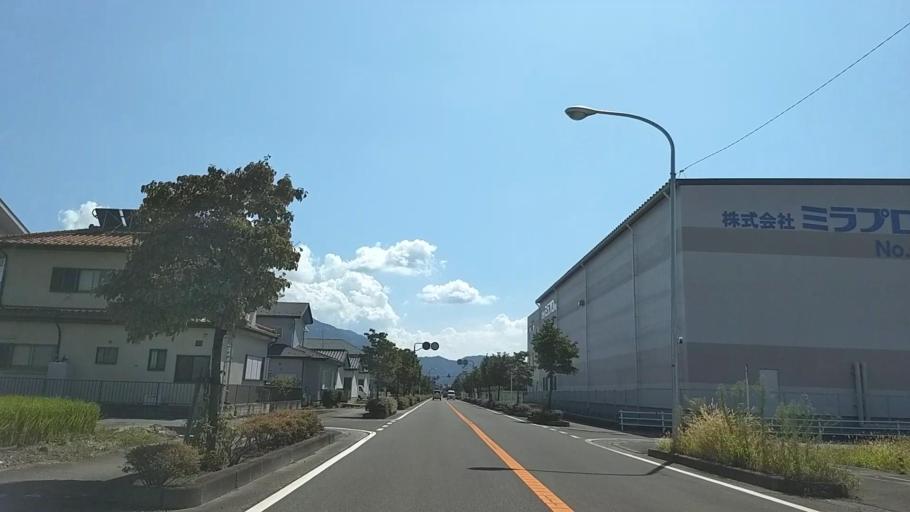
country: JP
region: Yamanashi
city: Ryuo
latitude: 35.5986
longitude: 138.5040
